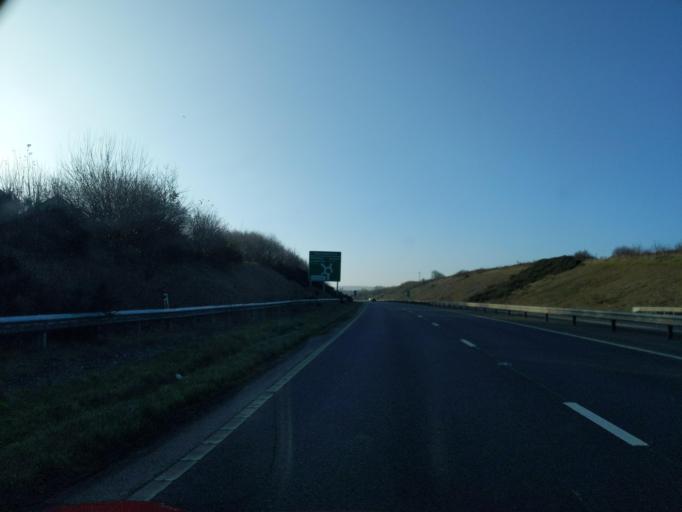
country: GB
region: England
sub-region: Cornwall
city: Liskeard
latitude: 50.4600
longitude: -4.5203
